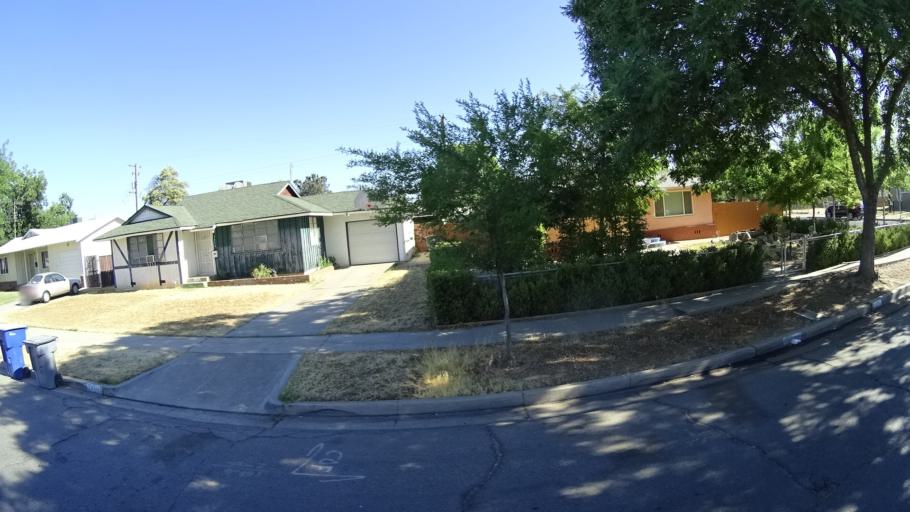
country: US
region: California
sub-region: Fresno County
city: Fresno
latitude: 36.7902
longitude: -119.8279
